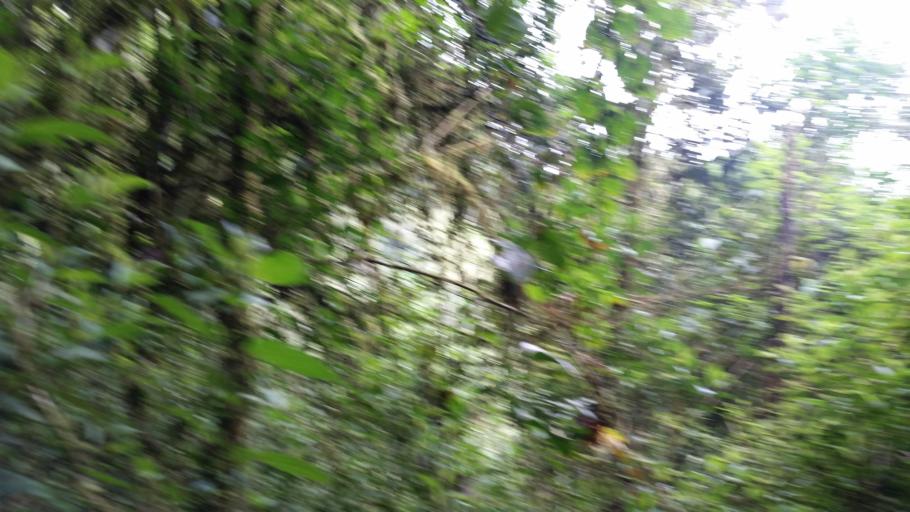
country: CO
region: Cundinamarca
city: Choachi
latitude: 4.5942
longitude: -73.9573
